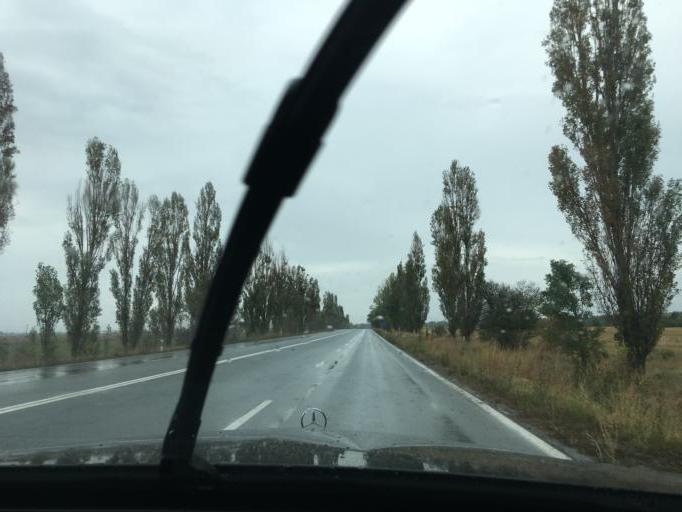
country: BG
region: Sofiya
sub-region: Obshtina Kostinbrod
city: Kostinbrod
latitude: 42.8064
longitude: 23.1265
